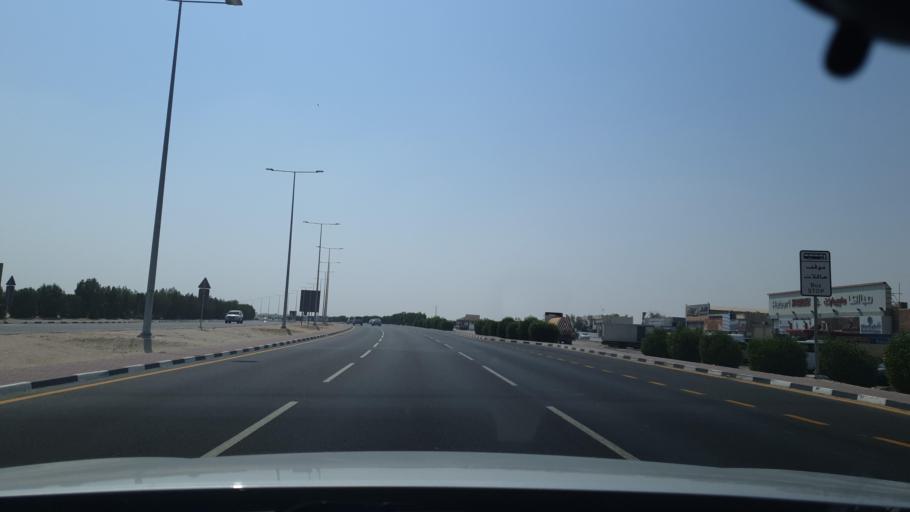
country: QA
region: Al Khawr
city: Al Khawr
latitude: 25.7122
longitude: 51.5069
